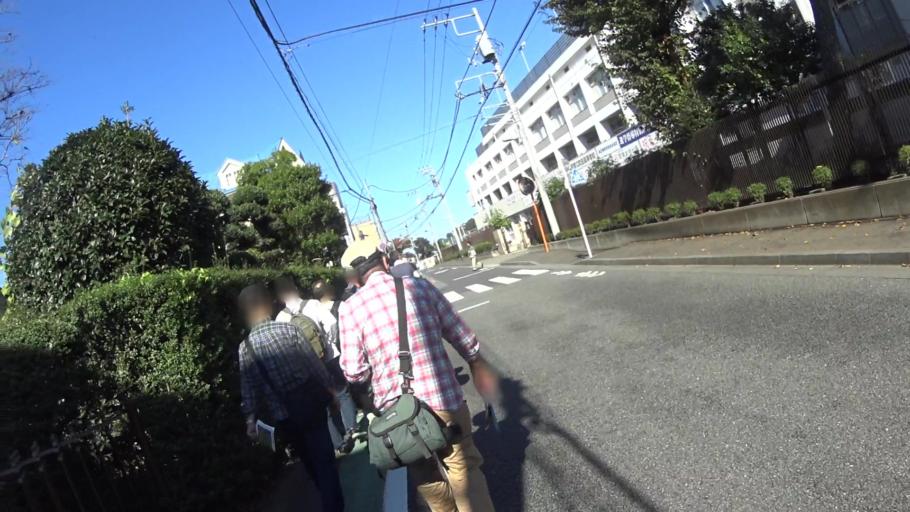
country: JP
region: Tokyo
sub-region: Machida-shi
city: Machida
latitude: 35.5540
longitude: 139.4486
